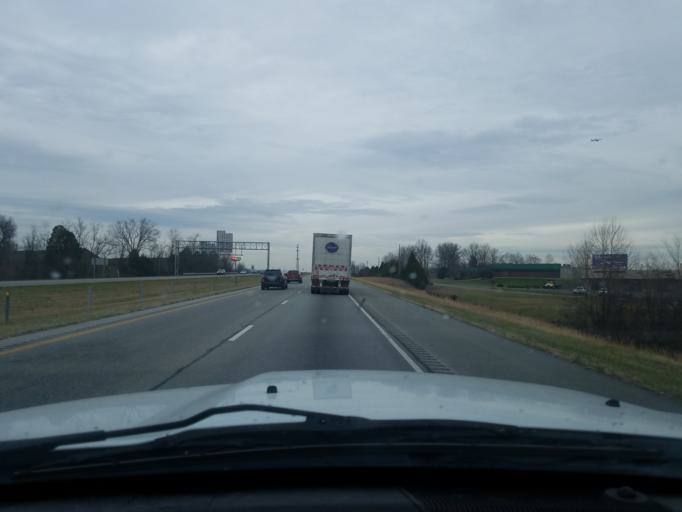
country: US
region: Indiana
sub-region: Floyd County
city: New Albany
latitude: 38.3298
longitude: -85.8288
